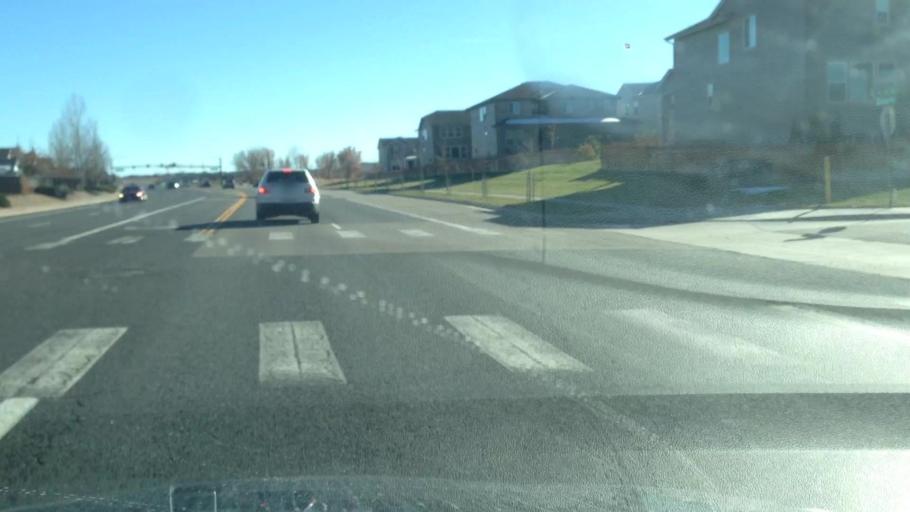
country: US
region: Colorado
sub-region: Douglas County
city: Stonegate
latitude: 39.5571
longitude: -104.7955
